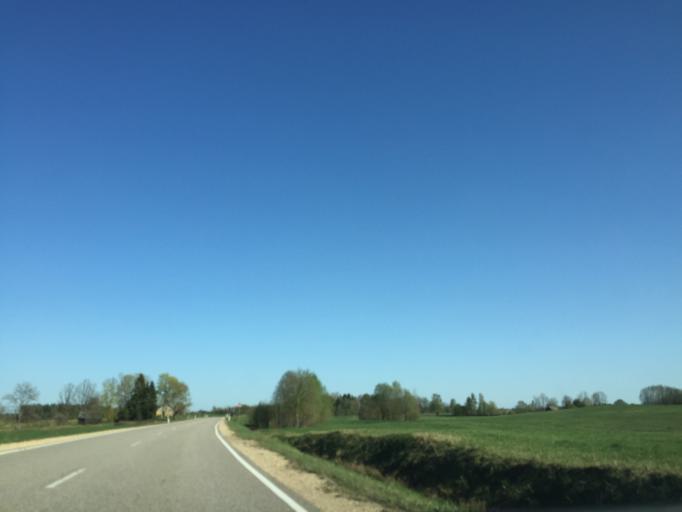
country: LV
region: Ergli
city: Ergli
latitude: 56.9011
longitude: 25.4646
